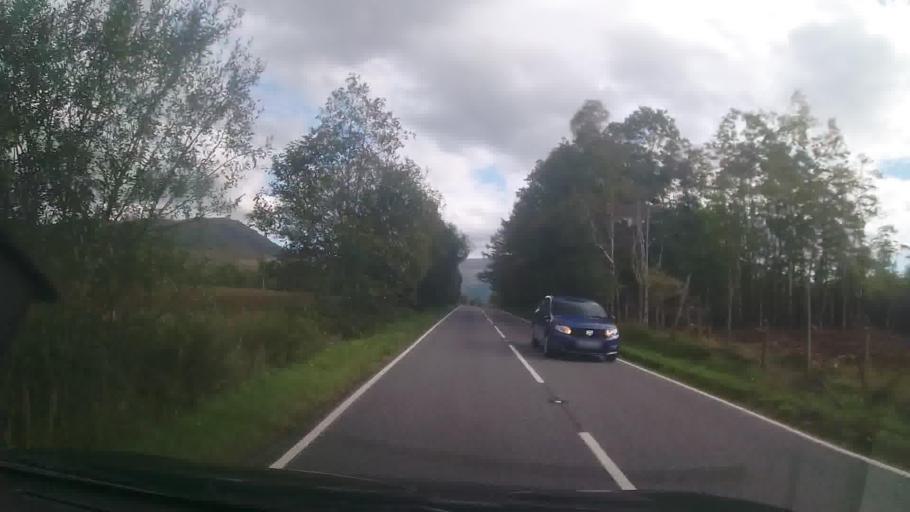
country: GB
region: Scotland
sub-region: Argyll and Bute
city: Oban
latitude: 56.5559
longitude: -5.3375
